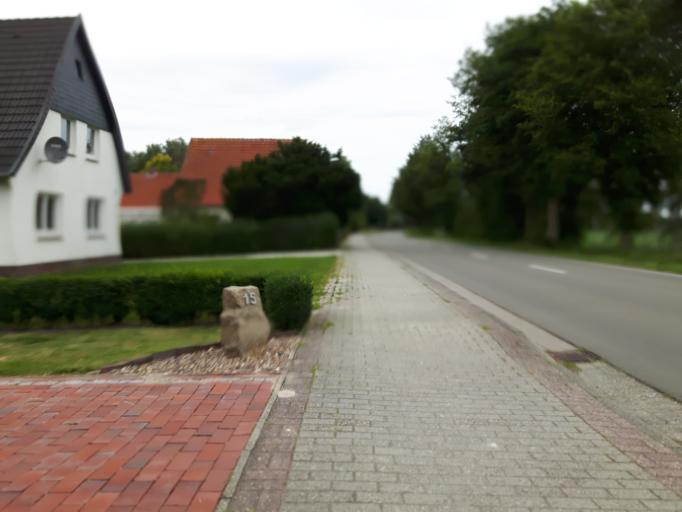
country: DE
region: Lower Saxony
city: Varel
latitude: 53.3868
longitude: 8.2411
